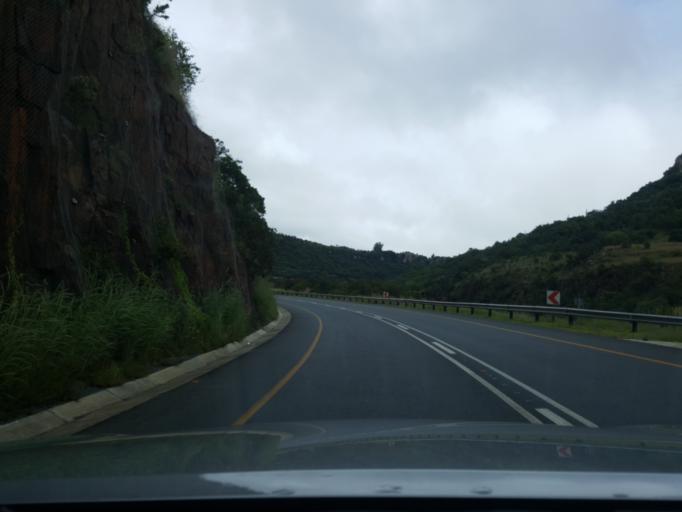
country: ZA
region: Mpumalanga
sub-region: Nkangala District Municipality
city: Belfast
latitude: -25.6450
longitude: 30.3574
